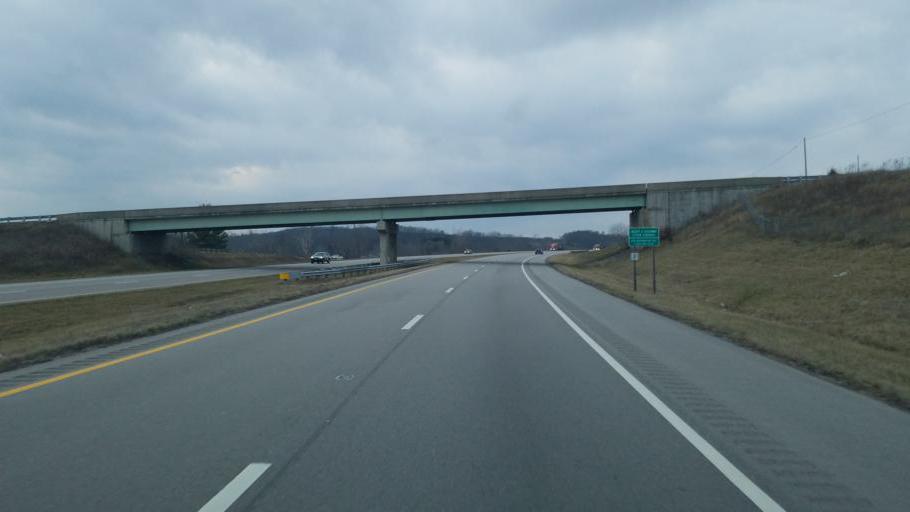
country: US
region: Ohio
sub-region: Jackson County
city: Oak Hill
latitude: 38.8847
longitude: -82.4201
